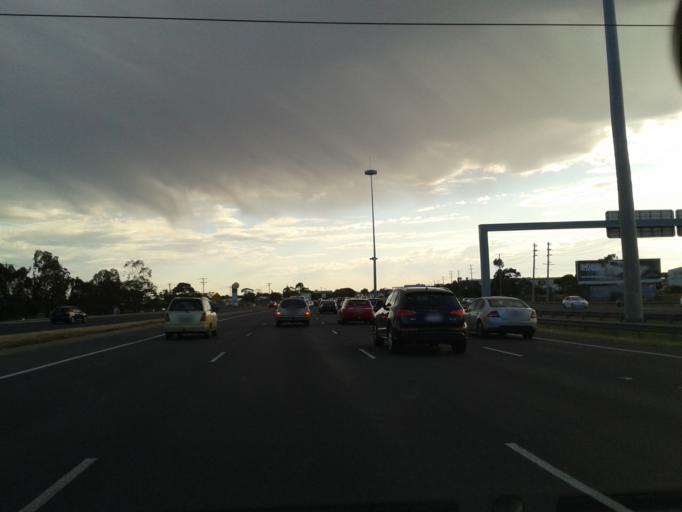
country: AU
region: Victoria
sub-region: Brimbank
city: Brooklyn
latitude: -37.8314
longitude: 144.8131
